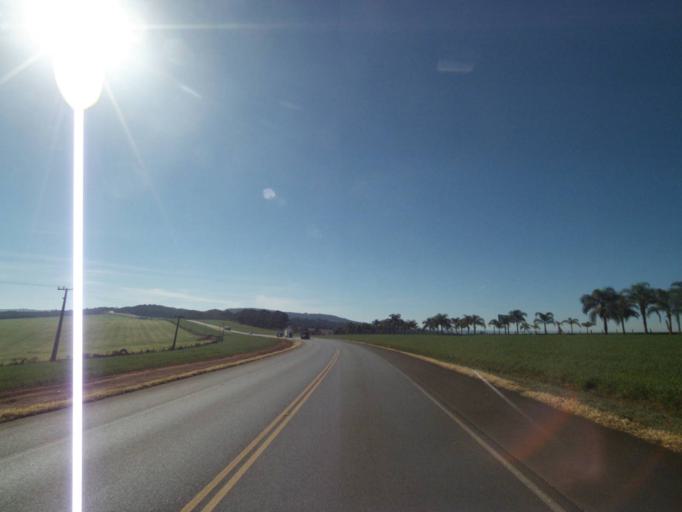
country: BR
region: Parana
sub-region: Tibagi
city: Tibagi
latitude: -24.4234
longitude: -50.3758
